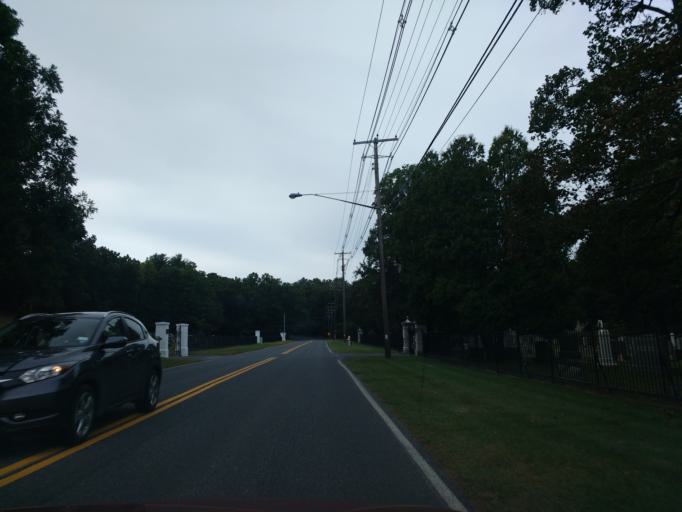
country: US
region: New York
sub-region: Ulster County
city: Kingston
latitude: 41.9217
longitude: -74.0026
